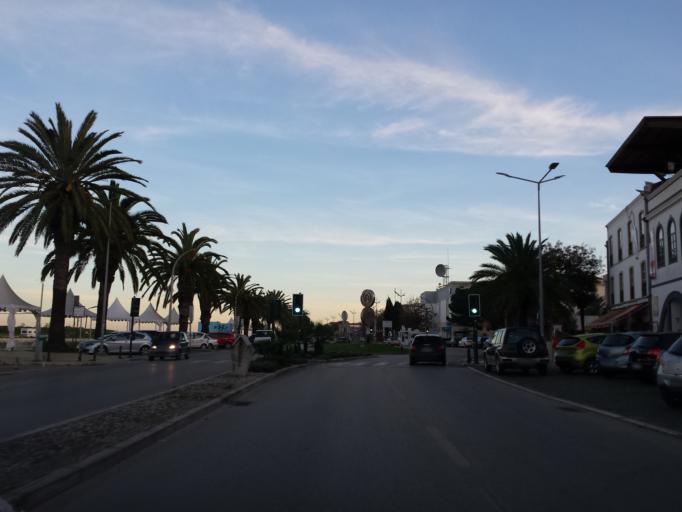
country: PT
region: Faro
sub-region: Lagos
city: Lagos
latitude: 37.1044
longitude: -8.6730
